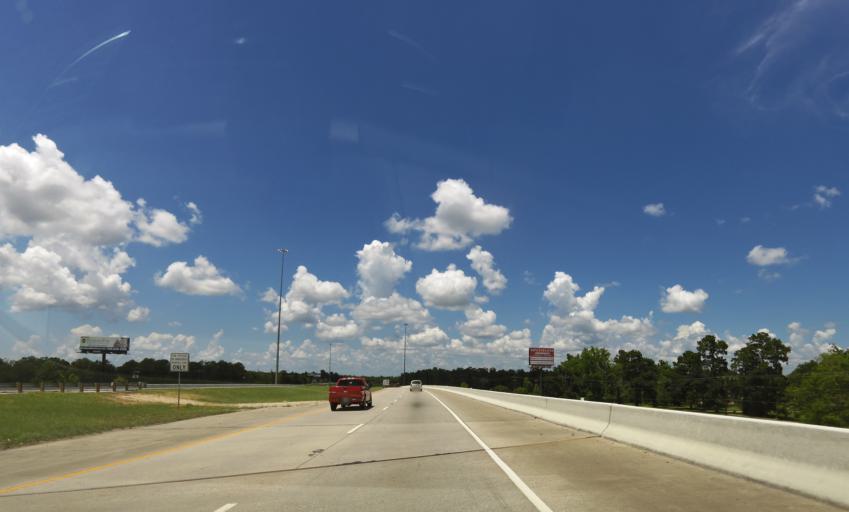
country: US
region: Texas
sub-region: San Jacinto County
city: Shepherd
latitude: 30.5011
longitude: -94.9878
